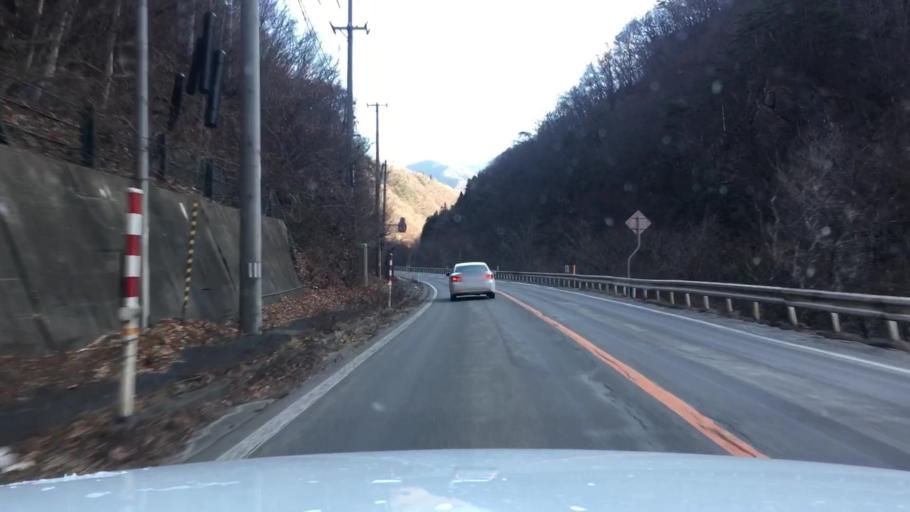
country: JP
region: Iwate
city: Tono
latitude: 39.6475
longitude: 141.5718
